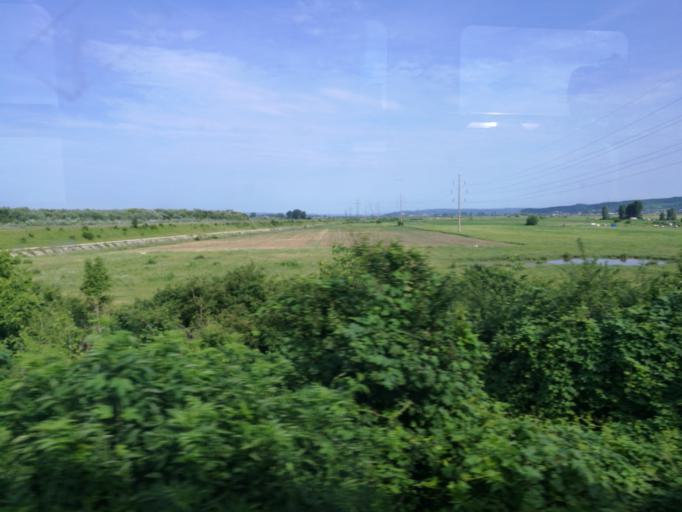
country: RO
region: Arges
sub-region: Oras Stefanesti
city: Golesti
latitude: 44.8303
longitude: 24.9367
